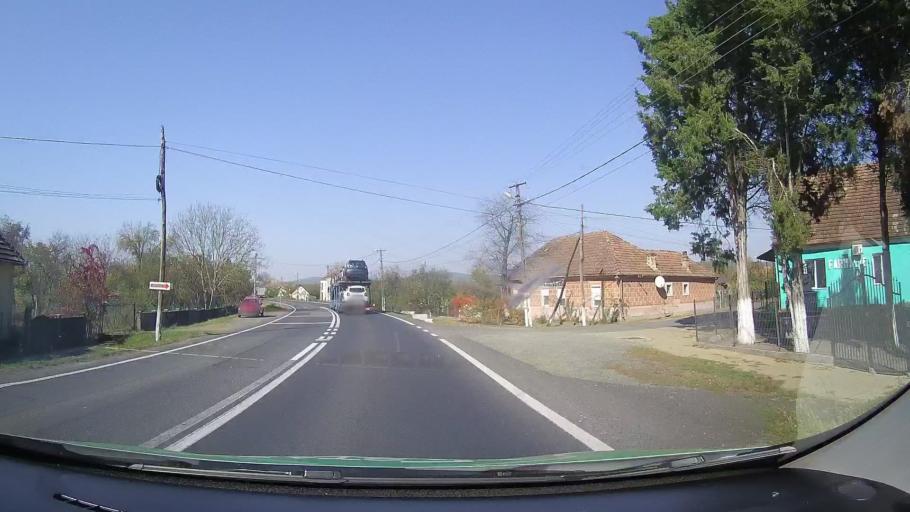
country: RO
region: Arad
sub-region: Comuna Varadia de Mures
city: Varadia de Mures
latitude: 46.0024
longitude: 22.1617
